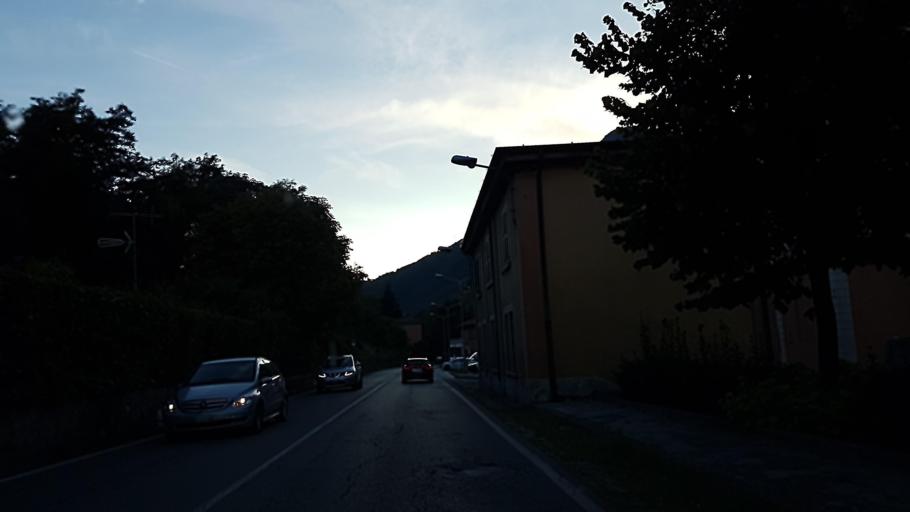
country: IT
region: Lombardy
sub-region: Provincia di Brescia
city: Roe
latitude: 45.6236
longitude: 10.4933
